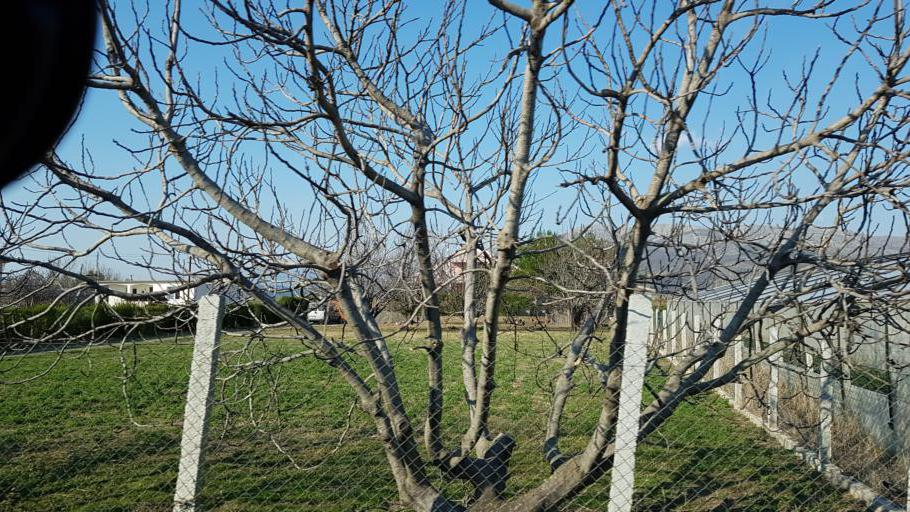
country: AL
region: Shkoder
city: Vukatane
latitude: 41.9923
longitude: 19.5630
